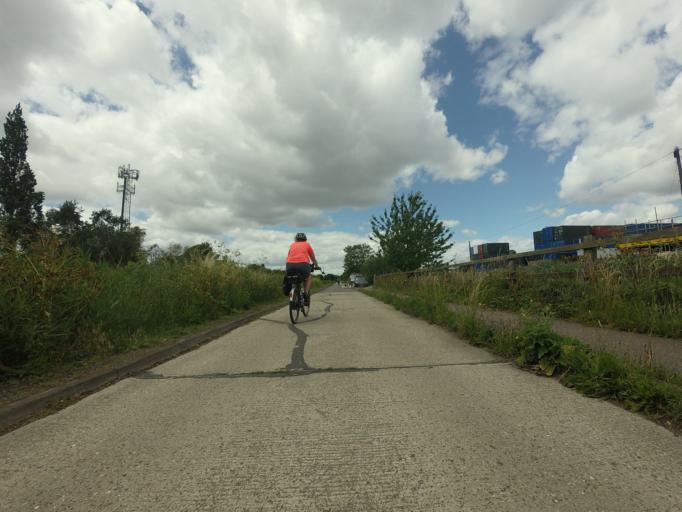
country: GB
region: England
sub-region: Kent
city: Gravesend
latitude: 51.4413
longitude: 0.3972
